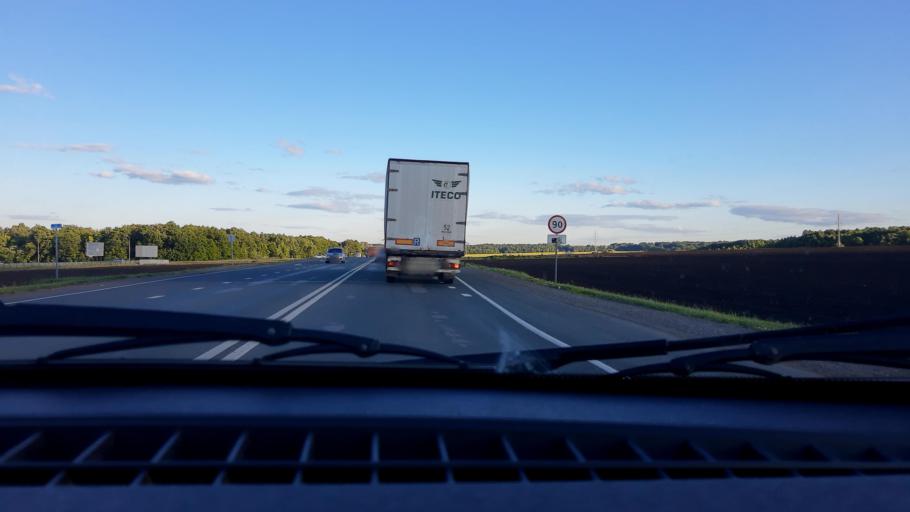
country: RU
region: Bashkortostan
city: Avdon
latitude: 54.7444
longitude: 55.7832
